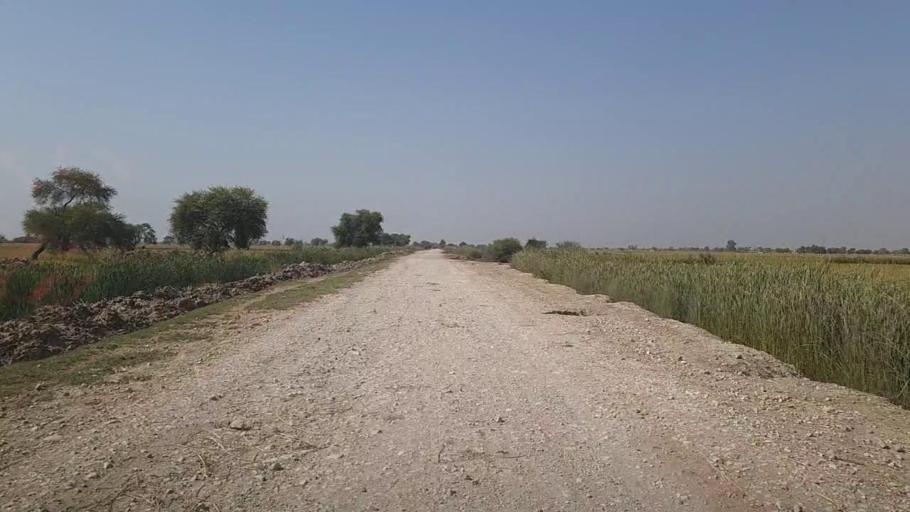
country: PK
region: Sindh
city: Kandhkot
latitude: 28.3972
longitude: 69.2702
